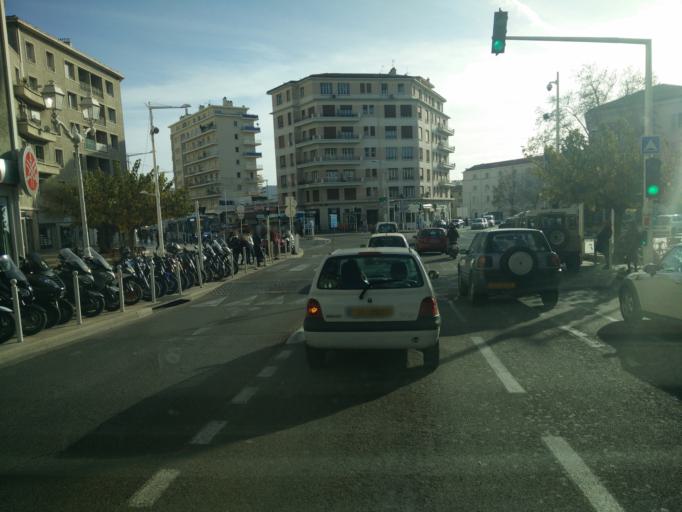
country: FR
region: Provence-Alpes-Cote d'Azur
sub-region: Departement du Var
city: Toulon
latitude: 43.1245
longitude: 5.9362
